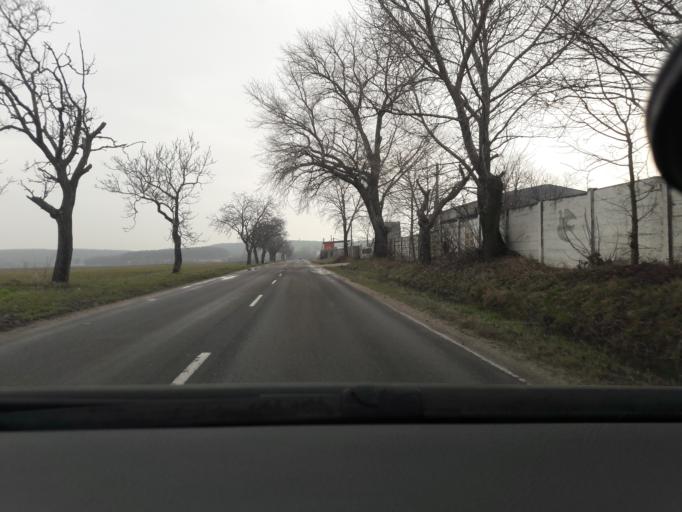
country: SK
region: Trnavsky
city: Smolenice
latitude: 48.4907
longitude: 17.4200
